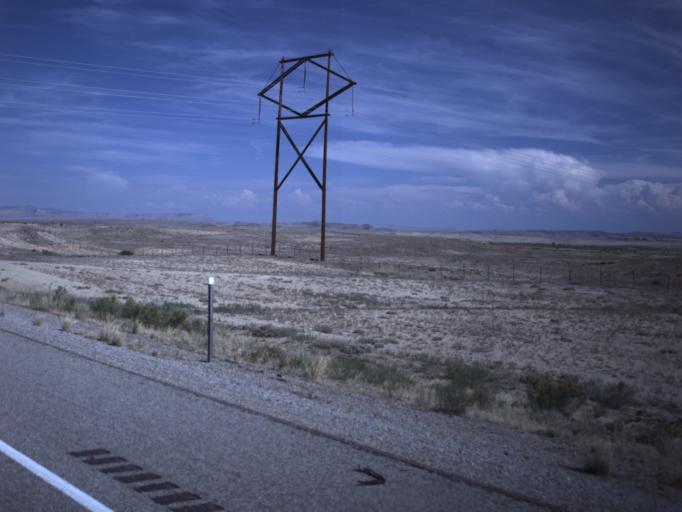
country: US
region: Utah
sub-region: Carbon County
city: East Carbon City
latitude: 38.9662
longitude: -110.2741
